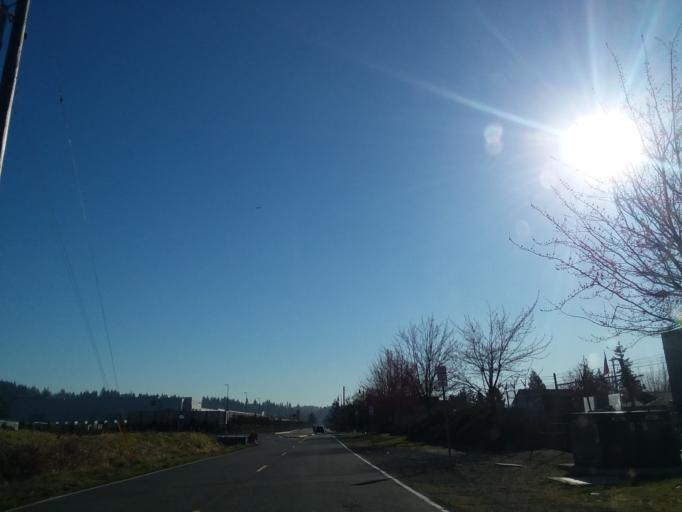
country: US
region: Washington
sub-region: Pierce County
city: Fife
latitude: 47.2463
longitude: -122.3688
